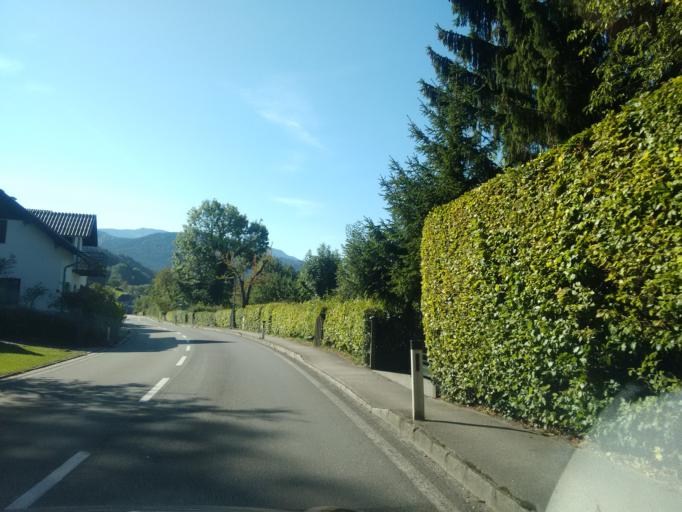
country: AT
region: Upper Austria
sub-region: Politischer Bezirk Vocklabruck
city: Attersee
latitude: 47.8900
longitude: 13.5679
